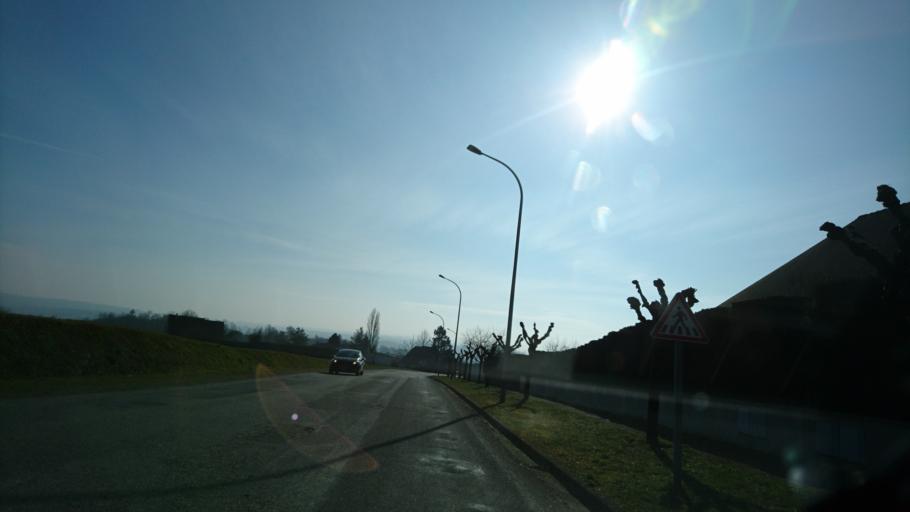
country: FR
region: Limousin
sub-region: Departement de la Haute-Vienne
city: Le Palais-sur-Vienne
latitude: 45.8741
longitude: 1.3097
